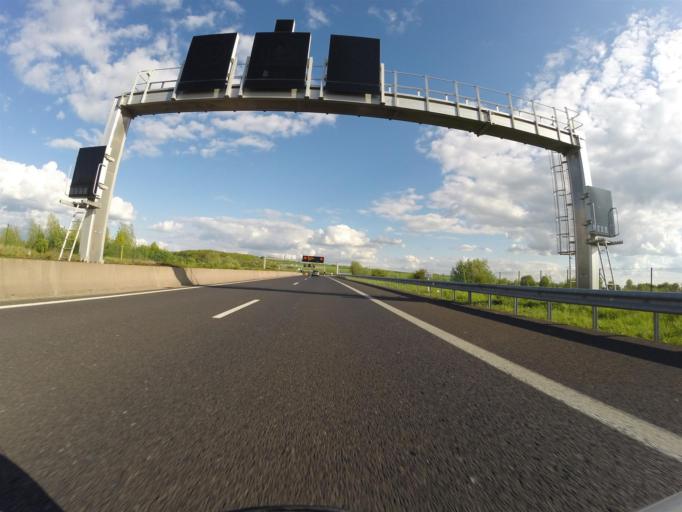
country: LU
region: Grevenmacher
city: Schengen
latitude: 49.4852
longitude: 6.3353
